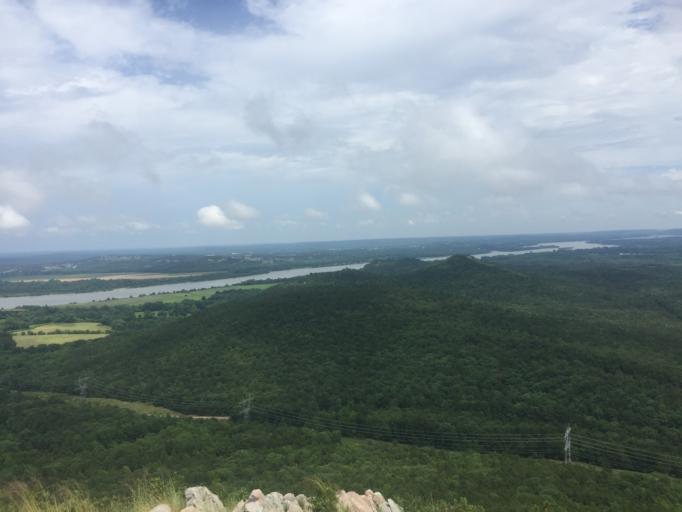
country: US
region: Arkansas
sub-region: Pulaski County
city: Maumelle
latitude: 34.8421
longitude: -92.4853
